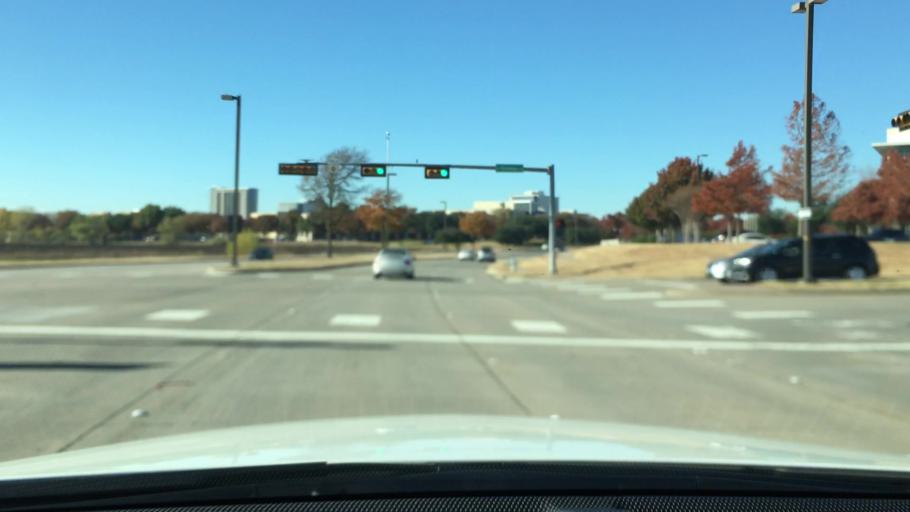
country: US
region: Texas
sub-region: Collin County
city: Frisco
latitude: 33.0849
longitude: -96.8119
